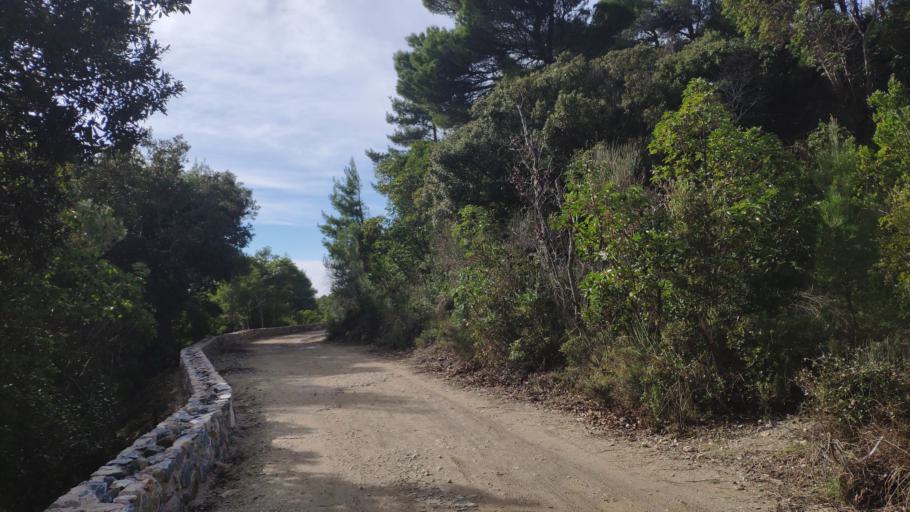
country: GR
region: Attica
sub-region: Nomarchia Anatolikis Attikis
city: Varybobi
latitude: 38.1655
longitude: 23.7800
